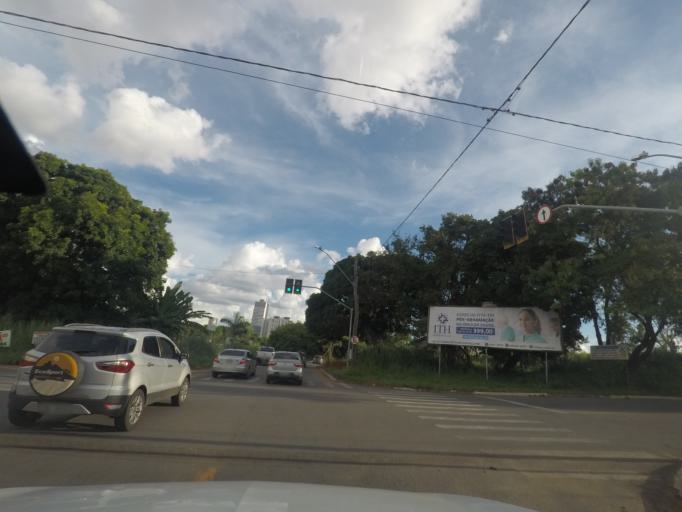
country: BR
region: Goias
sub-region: Goiania
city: Goiania
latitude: -16.6887
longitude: -49.2928
